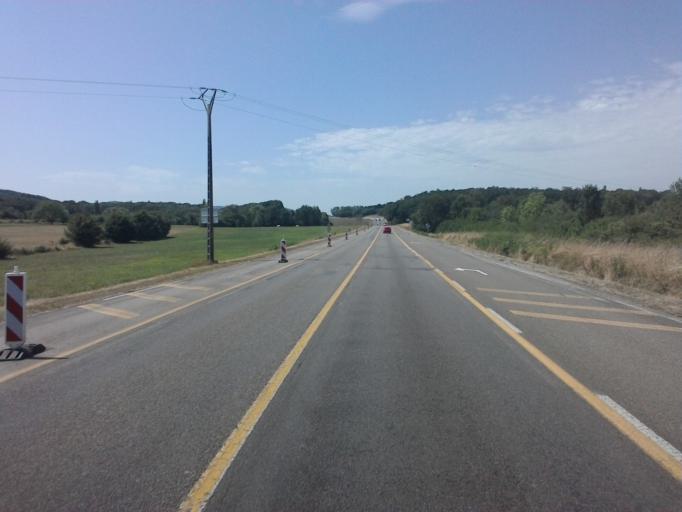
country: FR
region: Franche-Comte
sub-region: Departement du Jura
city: Montmorot
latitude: 46.6576
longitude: 5.5148
